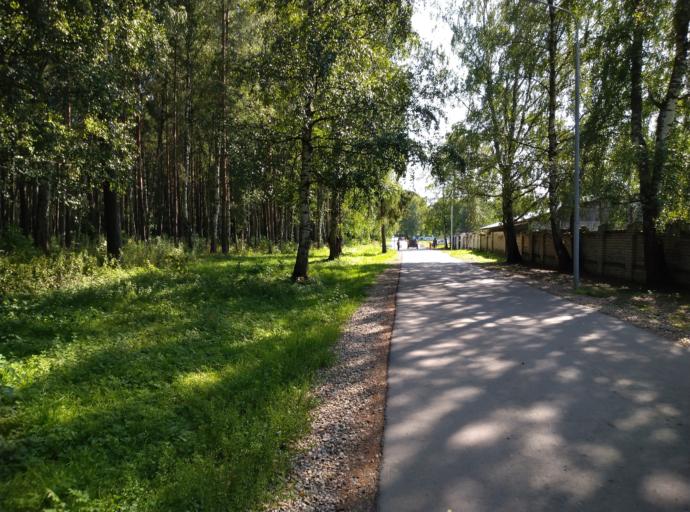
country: RU
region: Kostroma
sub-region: Kostromskoy Rayon
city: Kostroma
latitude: 57.7915
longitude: 40.9655
